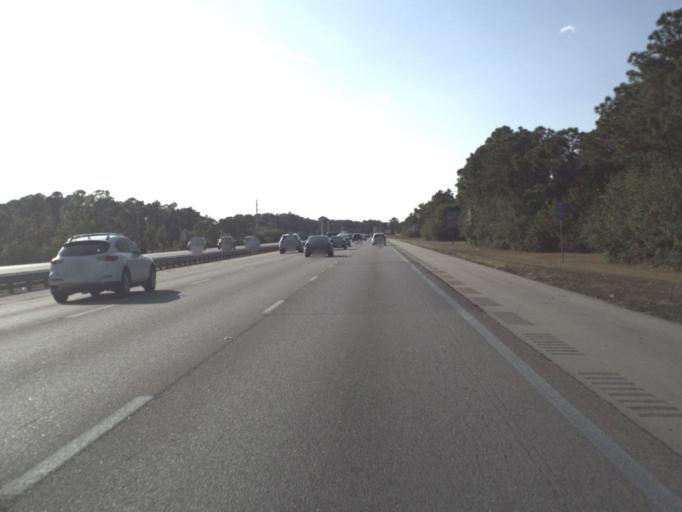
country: US
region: Florida
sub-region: Brevard County
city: June Park
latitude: 28.0656
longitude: -80.6967
